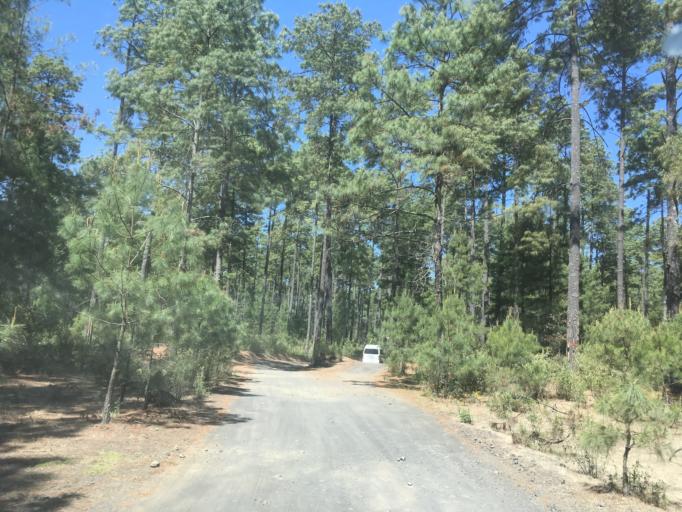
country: MX
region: Michoacan
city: Nuevo San Juan Parangaricutiro
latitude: 19.4597
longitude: -102.2076
